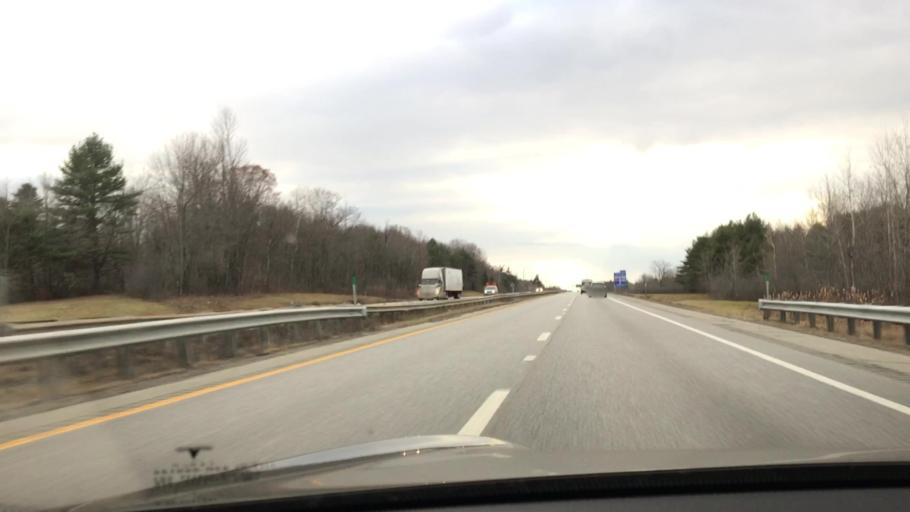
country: US
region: Maine
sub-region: Kennebec County
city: Gardiner
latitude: 44.2308
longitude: -69.8118
